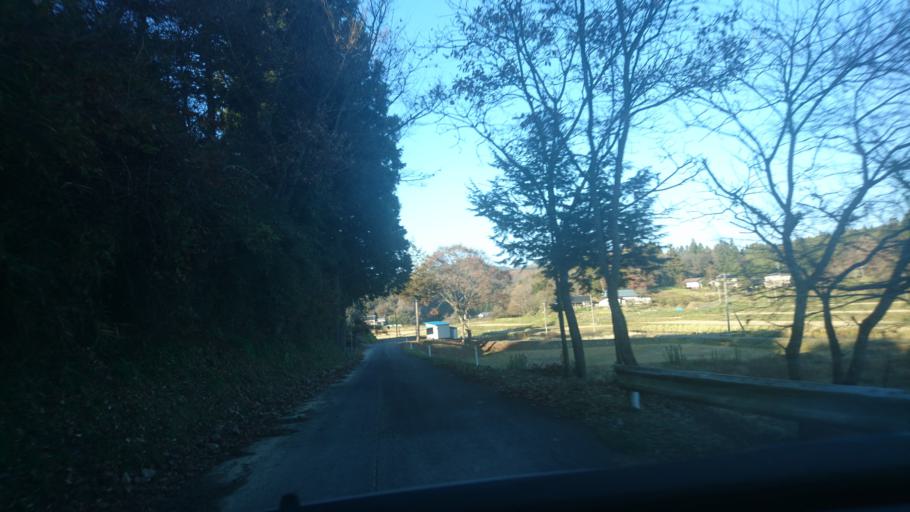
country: JP
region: Iwate
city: Ichinoseki
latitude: 38.9048
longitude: 141.2268
